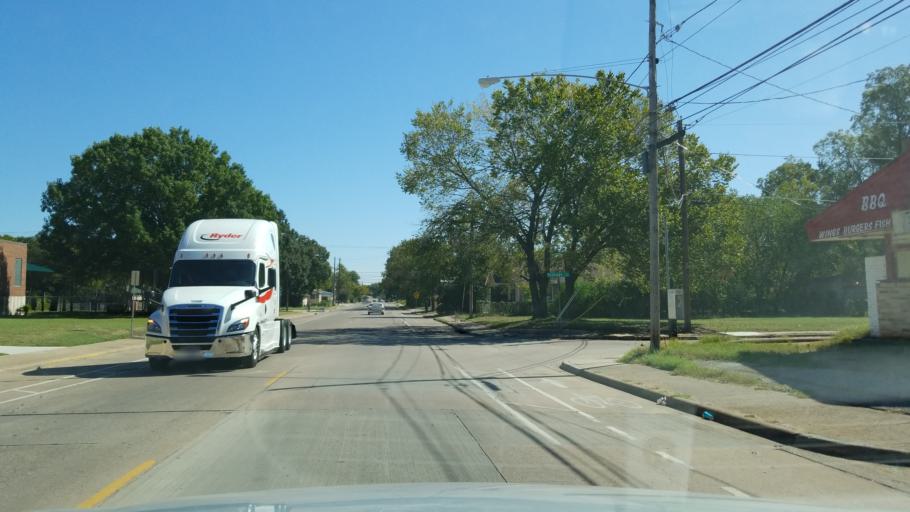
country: US
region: Texas
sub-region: Dallas County
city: Dallas
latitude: 32.7744
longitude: -96.7496
